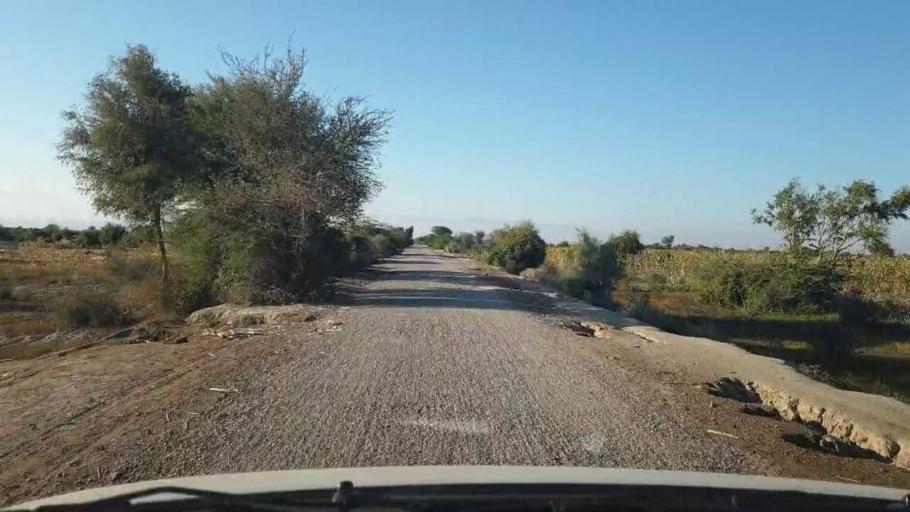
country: PK
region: Sindh
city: Johi
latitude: 26.7667
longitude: 67.4625
